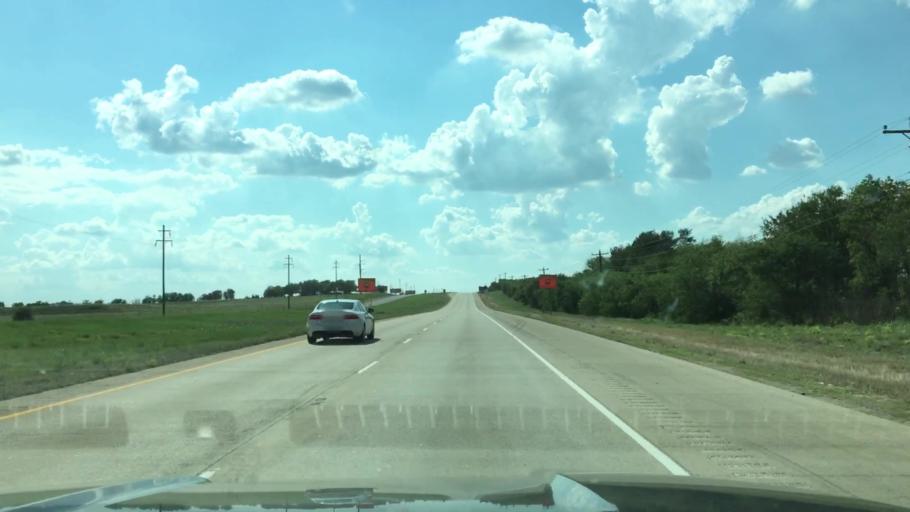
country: US
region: Texas
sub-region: Wise County
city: Rhome
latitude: 33.0369
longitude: -97.4113
